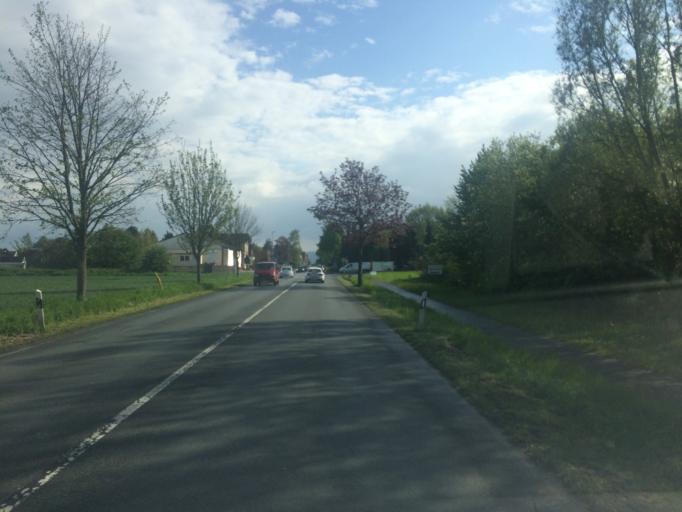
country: DE
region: Lower Saxony
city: Gross Munzel
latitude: 52.3718
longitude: 9.4796
